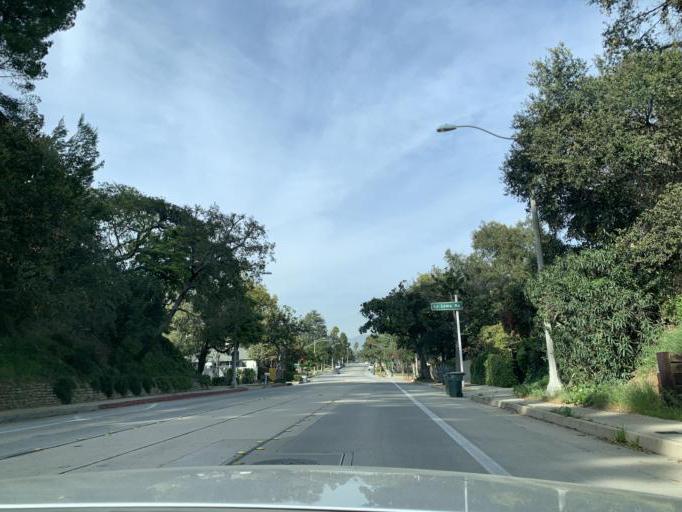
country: US
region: California
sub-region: Los Angeles County
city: South Pasadena
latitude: 34.1300
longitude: -118.1772
